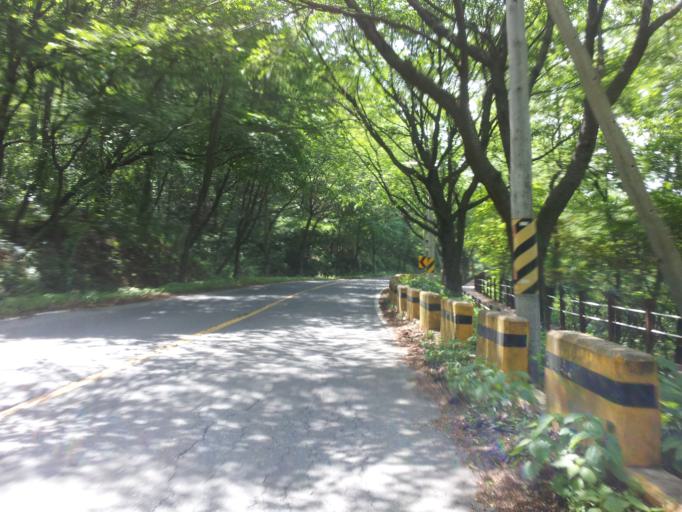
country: KR
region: Daejeon
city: Sintansin
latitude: 36.4374
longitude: 127.4718
